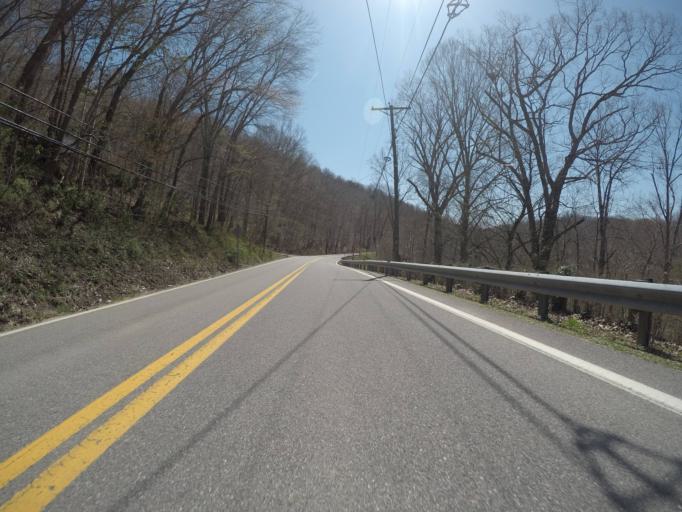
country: US
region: West Virginia
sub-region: Kanawha County
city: Pinch
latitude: 38.3957
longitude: -81.5540
